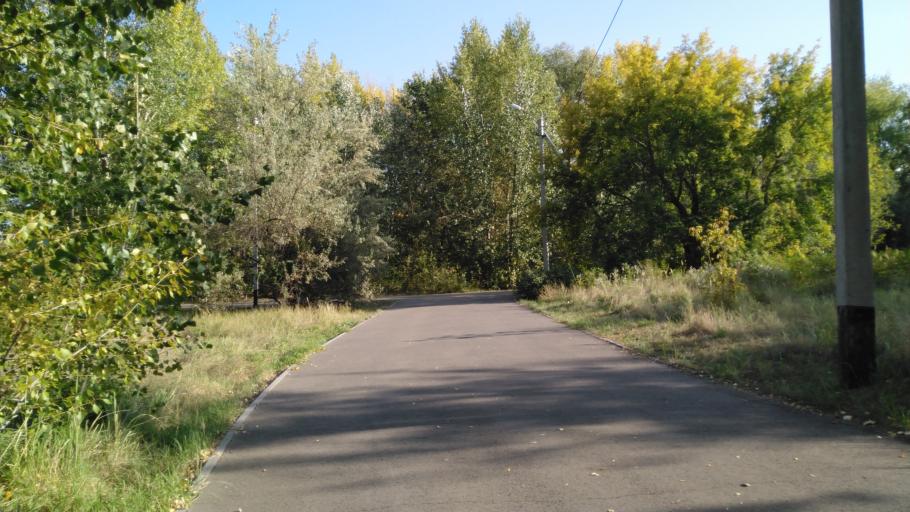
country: KZ
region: Pavlodar
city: Pavlodar
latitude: 52.2640
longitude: 76.9316
